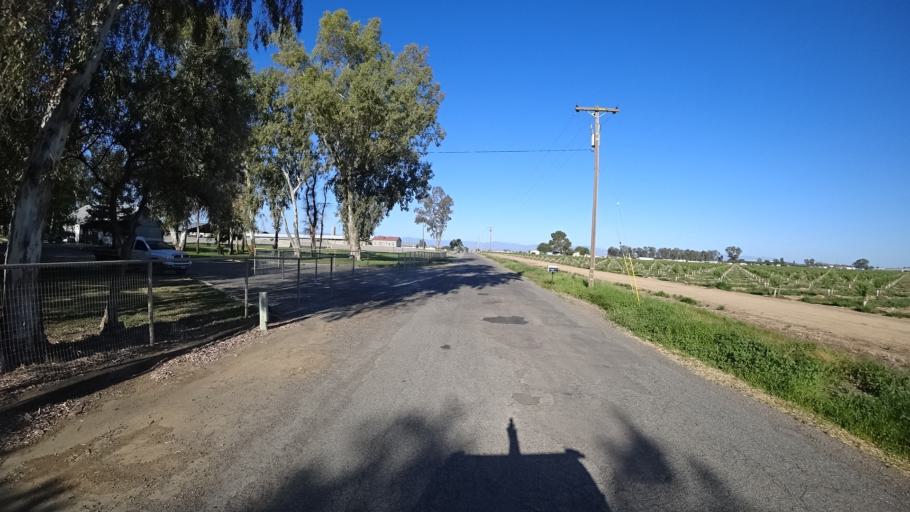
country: US
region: California
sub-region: Glenn County
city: Orland
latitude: 39.6822
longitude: -122.1894
